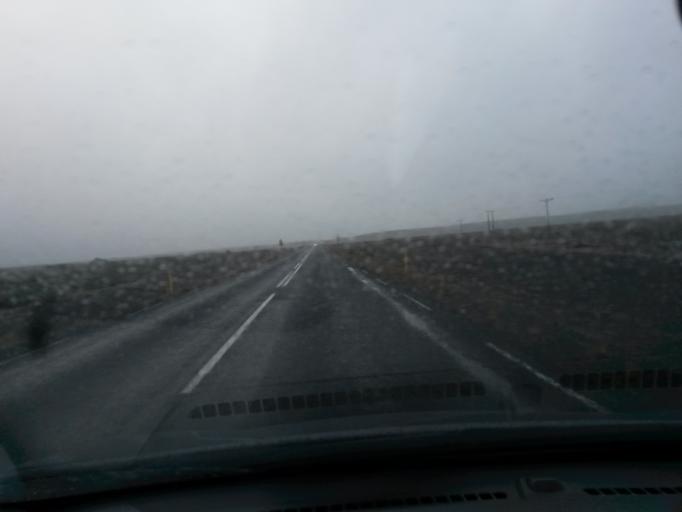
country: IS
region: South
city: Vestmannaeyjar
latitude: 63.4971
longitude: -19.3927
